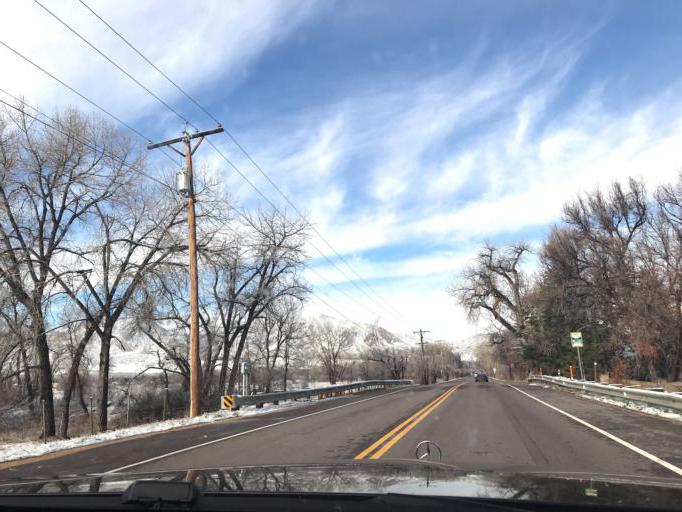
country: US
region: Colorado
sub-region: Boulder County
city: Boulder
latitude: 40.0001
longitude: -105.2148
